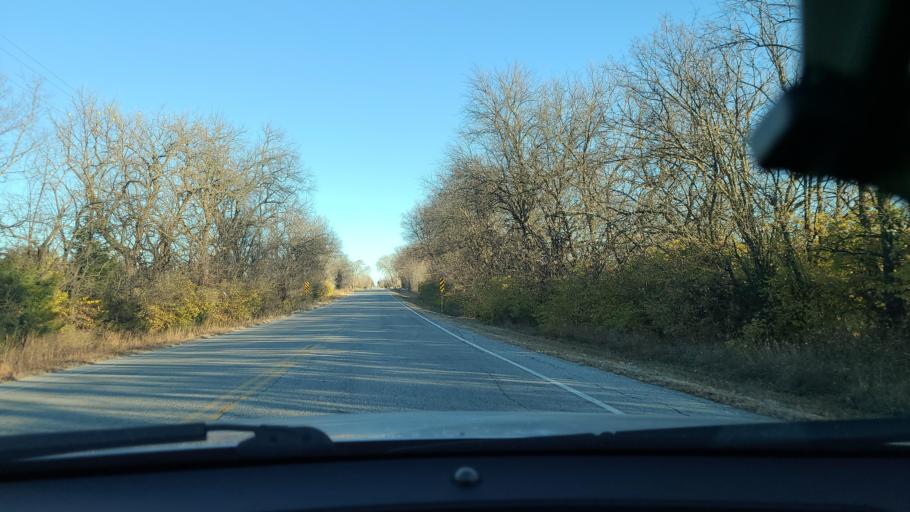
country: US
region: Kansas
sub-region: Sedgwick County
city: Park City
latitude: 37.8409
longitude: -97.3174
